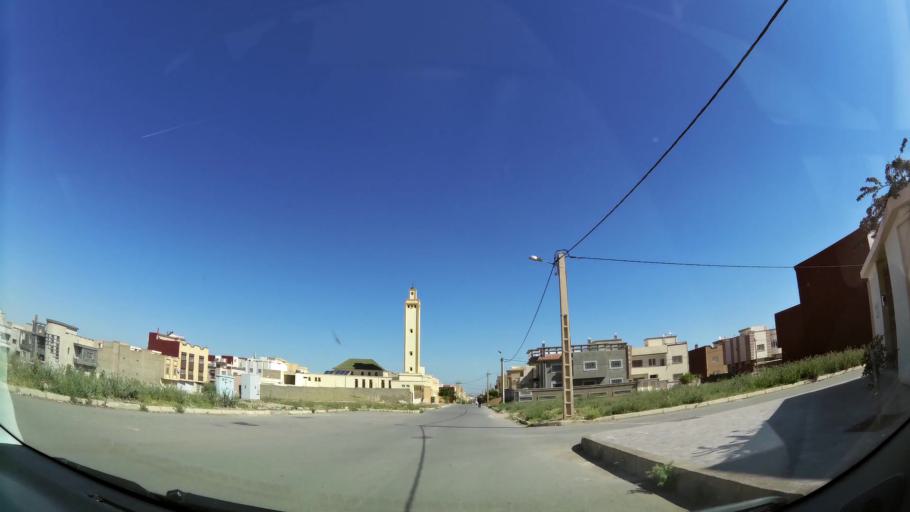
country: MA
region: Oriental
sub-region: Oujda-Angad
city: Oujda
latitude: 34.6540
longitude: -1.8865
